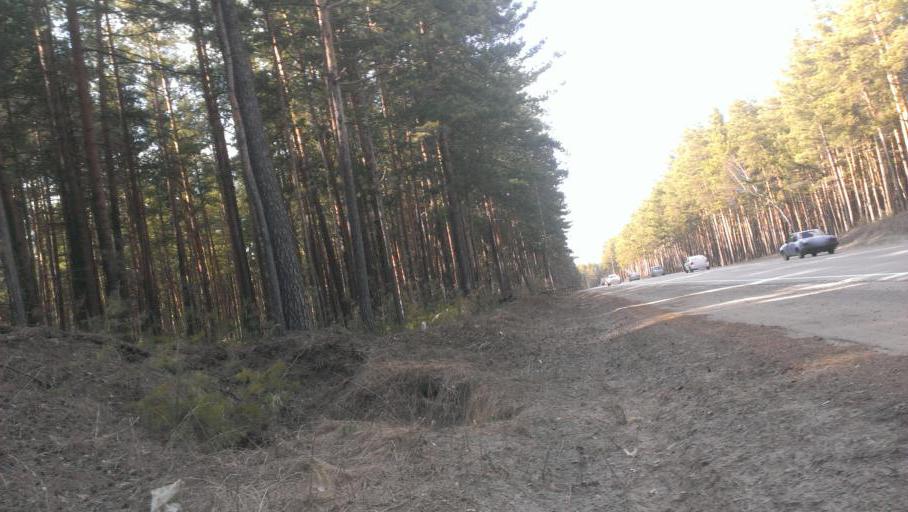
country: RU
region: Altai Krai
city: Yuzhnyy
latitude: 53.2939
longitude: 83.7059
